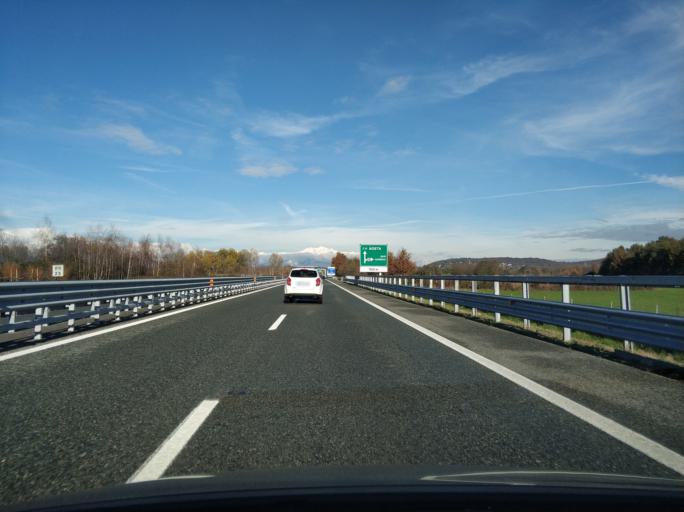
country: IT
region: Piedmont
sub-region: Provincia di Torino
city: San Giusto Canavese
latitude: 45.3081
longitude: 7.8187
